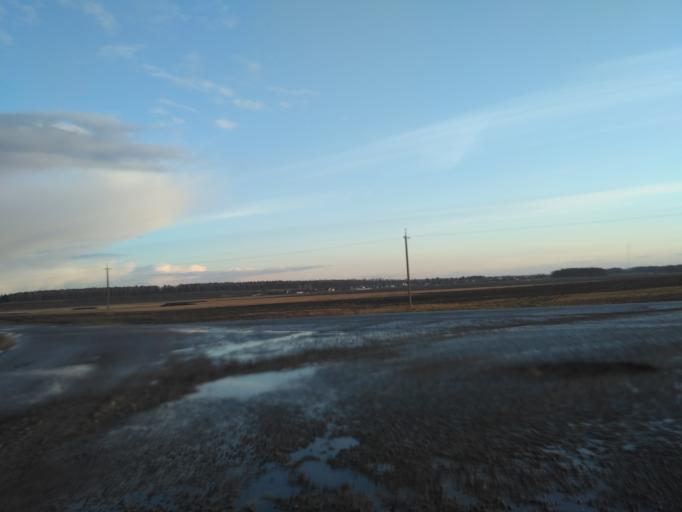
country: BY
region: Minsk
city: Slabada
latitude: 54.0041
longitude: 27.8710
